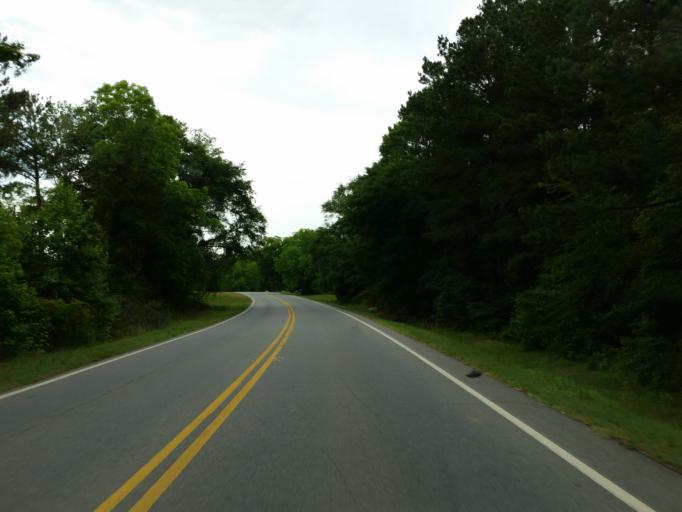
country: US
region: Georgia
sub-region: Dooly County
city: Vienna
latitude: 32.0804
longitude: -83.7934
